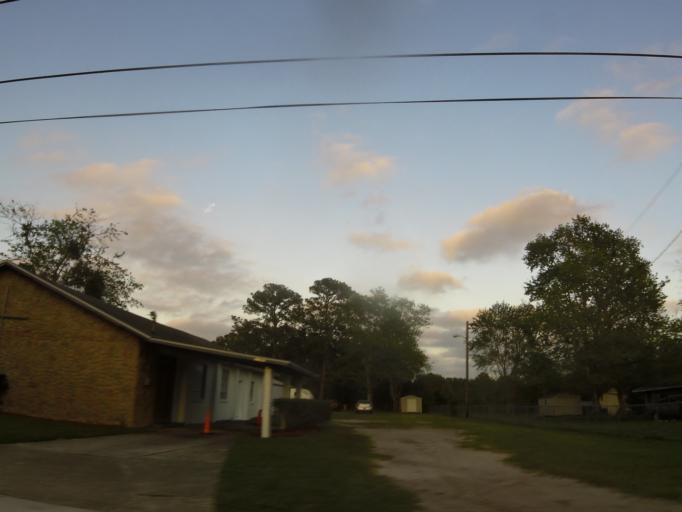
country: US
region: Florida
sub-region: Duval County
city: Jacksonville
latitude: 30.4688
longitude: -81.6261
